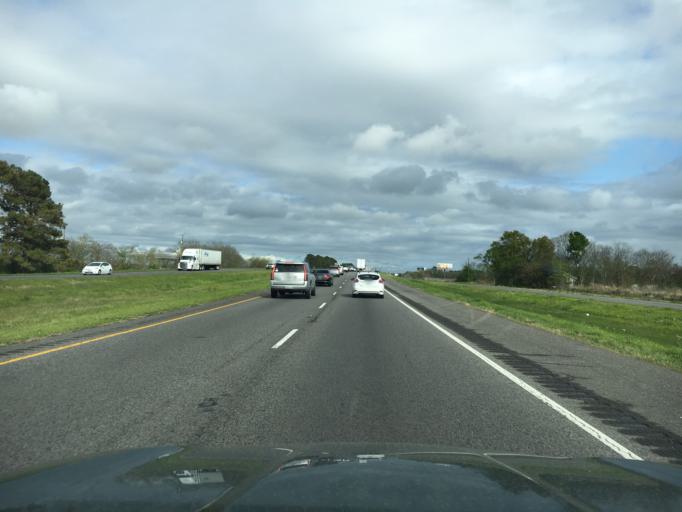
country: US
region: Louisiana
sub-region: Jefferson Davis Parish
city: Jennings
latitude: 30.2463
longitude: -92.7010
